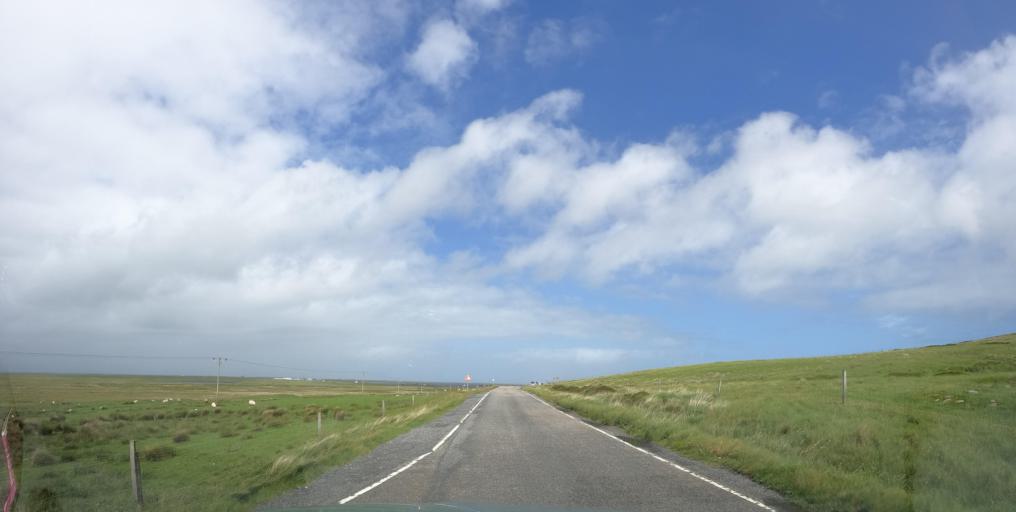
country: GB
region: Scotland
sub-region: Eilean Siar
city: Isle of South Uist
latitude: 57.3418
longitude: -7.3647
